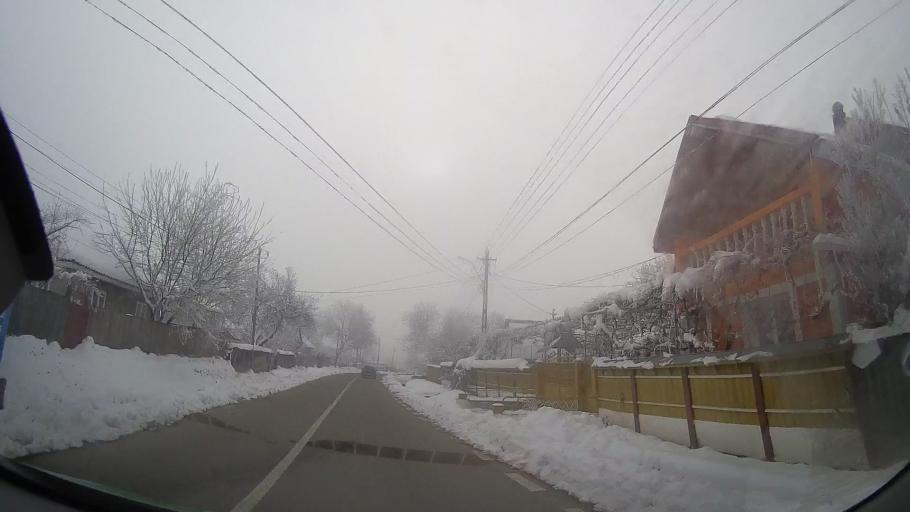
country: RO
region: Iasi
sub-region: Comuna Valea Seaca
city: Valea Seaca
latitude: 47.2914
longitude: 26.6665
